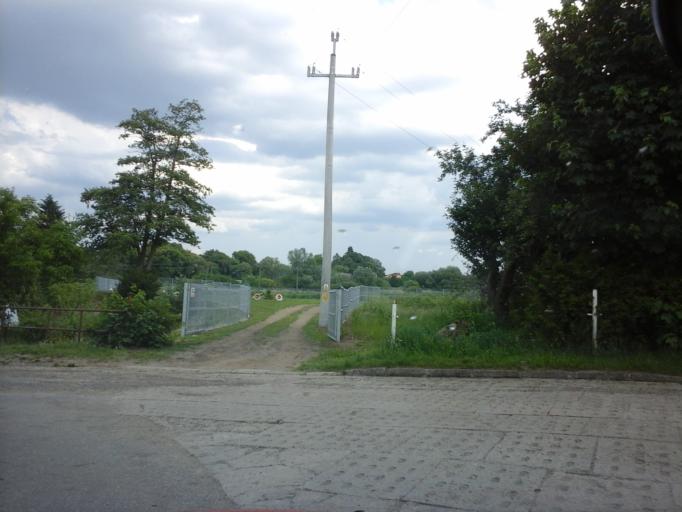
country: PL
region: West Pomeranian Voivodeship
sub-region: Powiat choszczenski
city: Recz
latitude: 53.2577
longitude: 15.5489
